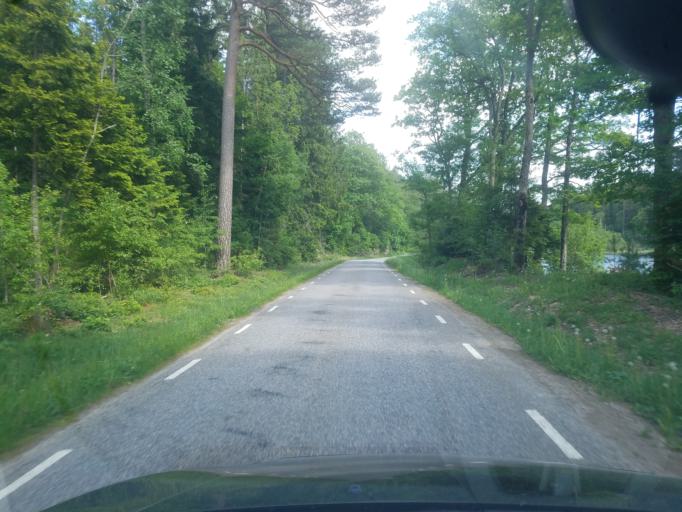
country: SE
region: Vaestra Goetaland
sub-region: Stenungsunds Kommun
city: Stora Hoga
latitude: 57.9982
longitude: 11.9383
